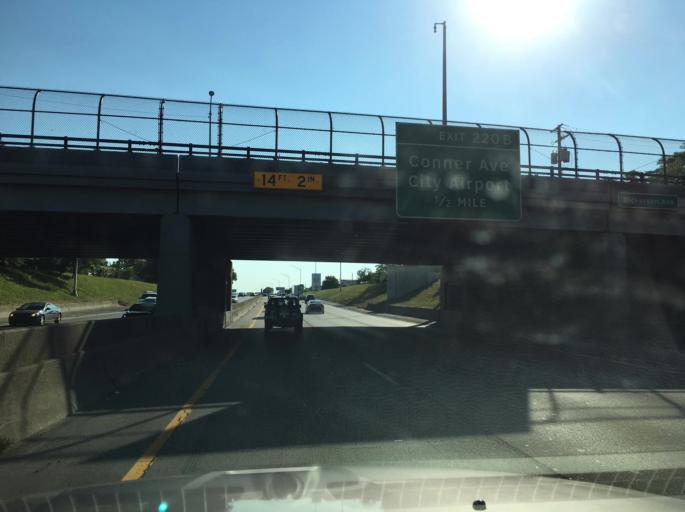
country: US
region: Michigan
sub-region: Wayne County
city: Grosse Pointe Park
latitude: 42.4017
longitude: -82.9726
